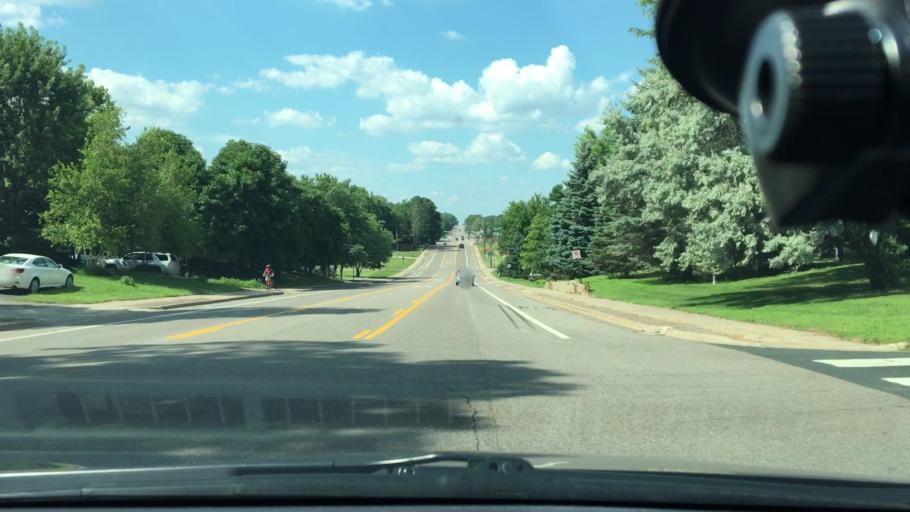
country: US
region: Minnesota
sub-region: Hennepin County
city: Golden Valley
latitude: 45.0018
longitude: -93.3803
